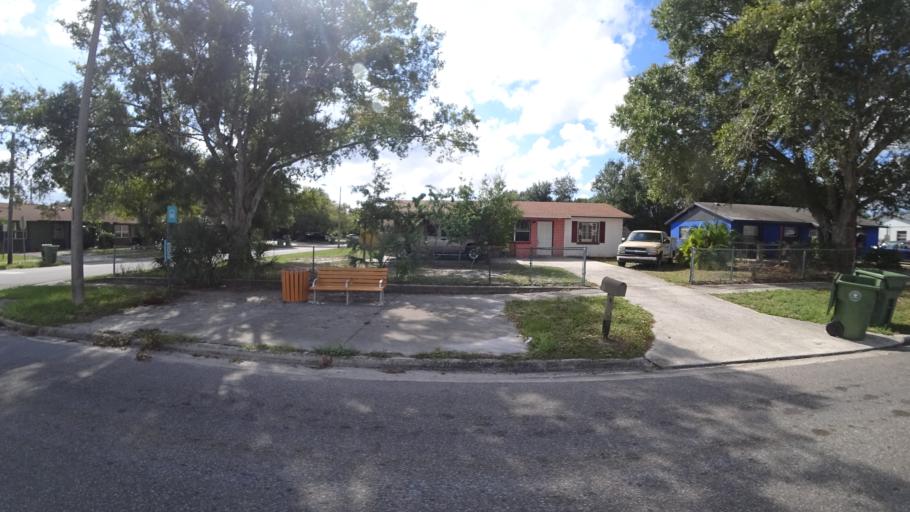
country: US
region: Florida
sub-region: Manatee County
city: Samoset
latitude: 27.4878
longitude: -82.5356
